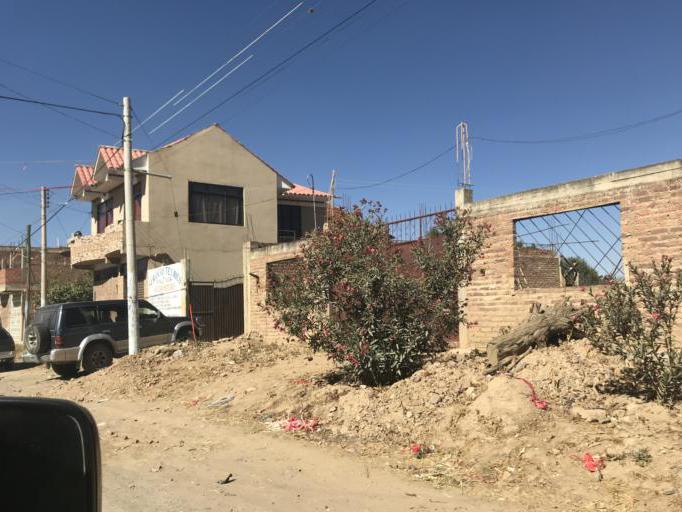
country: BO
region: Cochabamba
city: Cliza
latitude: -17.5897
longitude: -65.9271
